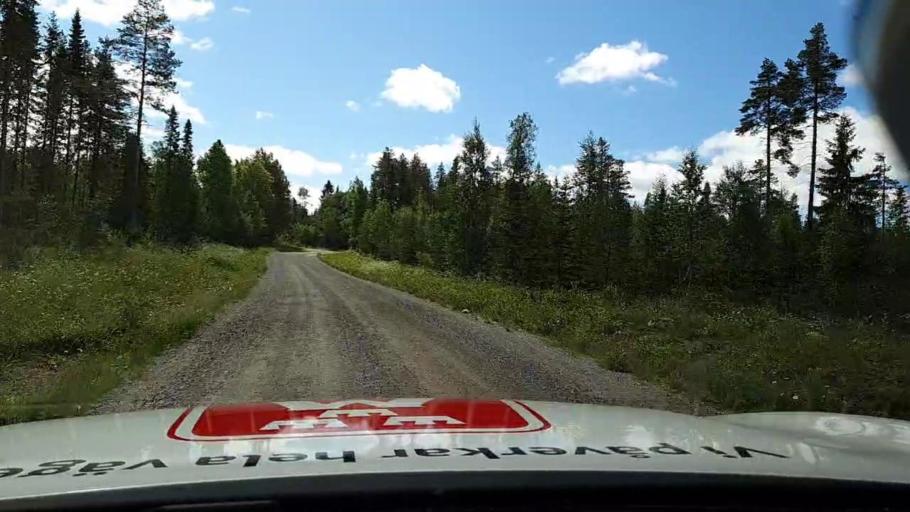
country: SE
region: Jaemtland
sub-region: Braecke Kommun
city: Braecke
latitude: 62.7467
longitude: 15.5023
